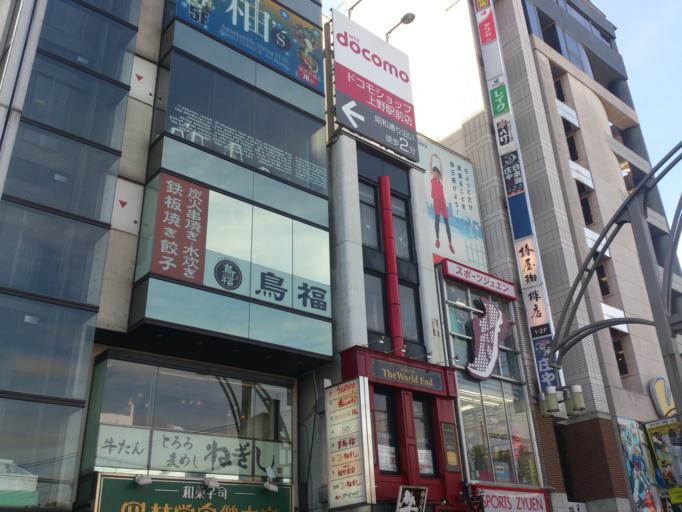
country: JP
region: Tokyo
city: Tokyo
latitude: 35.7115
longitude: 139.7757
